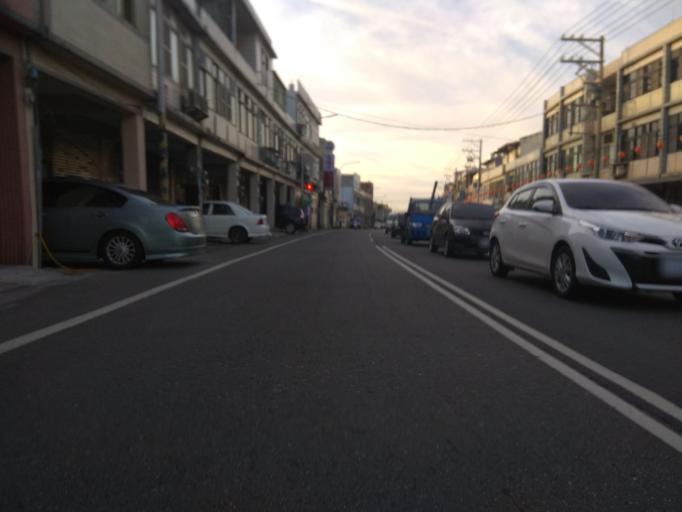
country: TW
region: Taiwan
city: Taoyuan City
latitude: 24.9957
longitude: 121.1636
